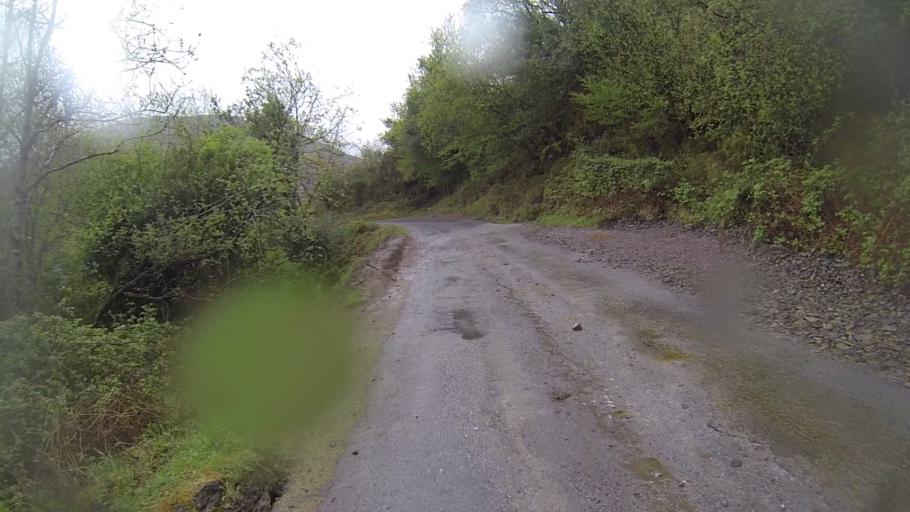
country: IE
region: Munster
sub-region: Ciarrai
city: Cill Airne
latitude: 52.0379
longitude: -9.6360
